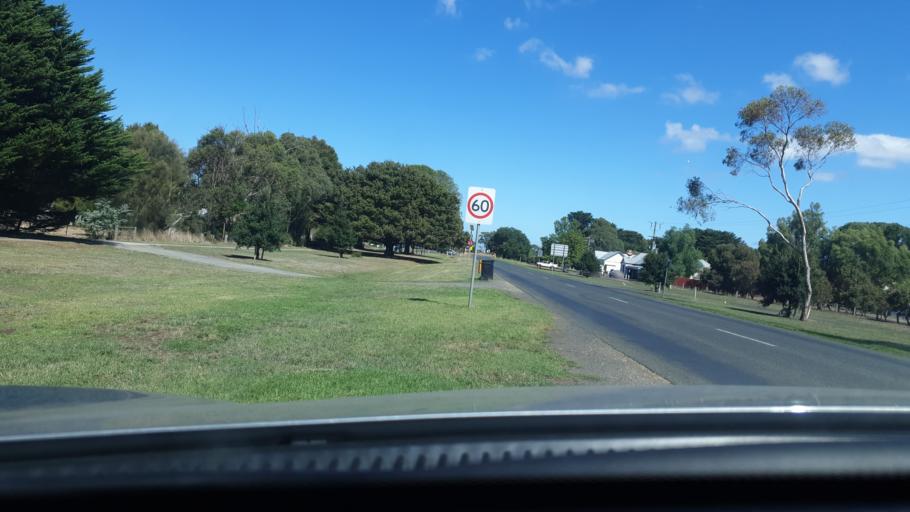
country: AU
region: Victoria
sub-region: Warrnambool
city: Warrnambool
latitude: -38.1850
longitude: 142.4317
